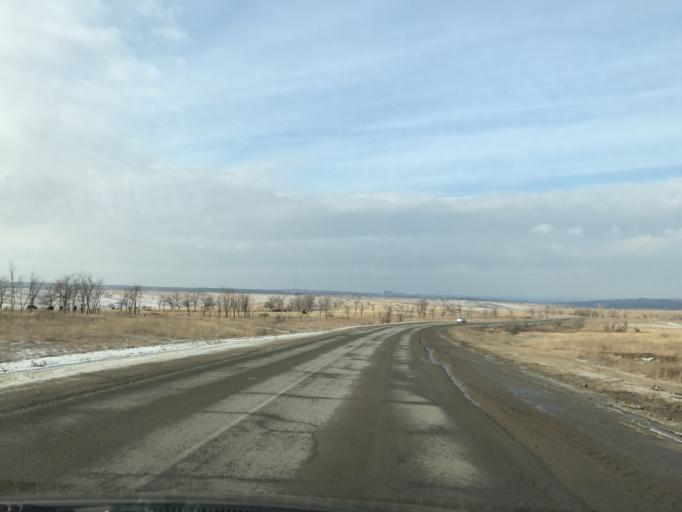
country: RU
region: Rostov
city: Staraya Stanitsa
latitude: 48.2709
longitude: 40.3501
